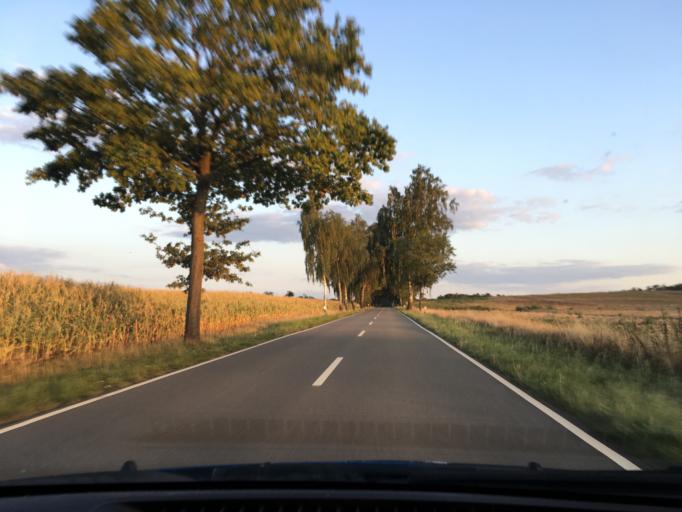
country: DE
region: Lower Saxony
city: Tosterglope
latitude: 53.2213
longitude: 10.8107
